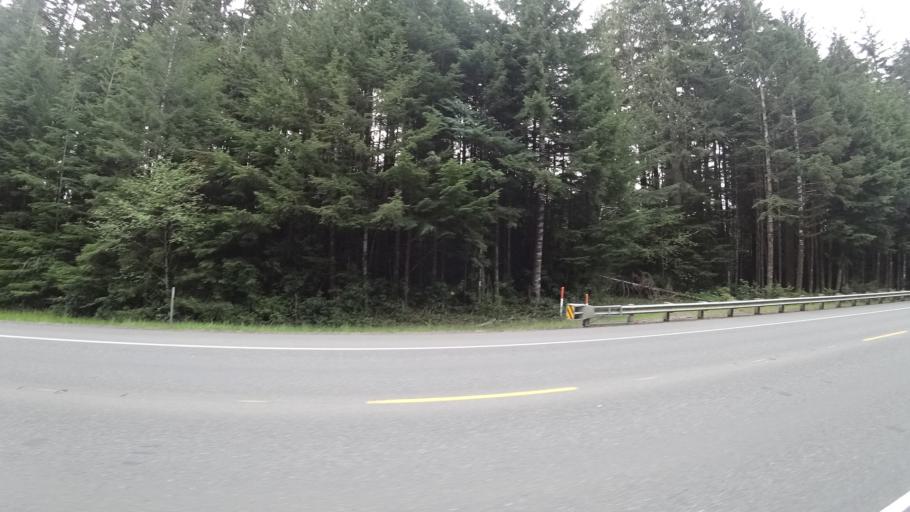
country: US
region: Oregon
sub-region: Coos County
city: Barview
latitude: 43.2511
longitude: -124.2864
